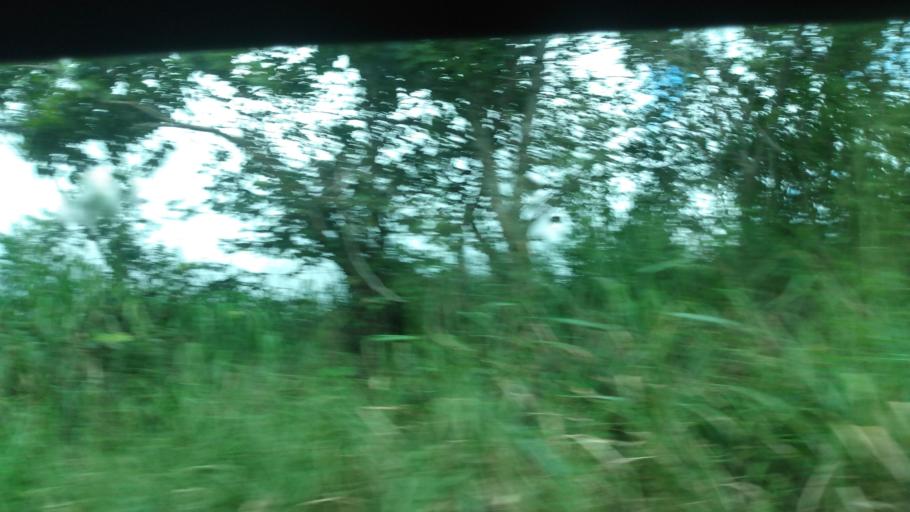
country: BR
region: Pernambuco
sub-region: Quipapa
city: Quipapa
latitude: -8.8047
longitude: -36.0062
